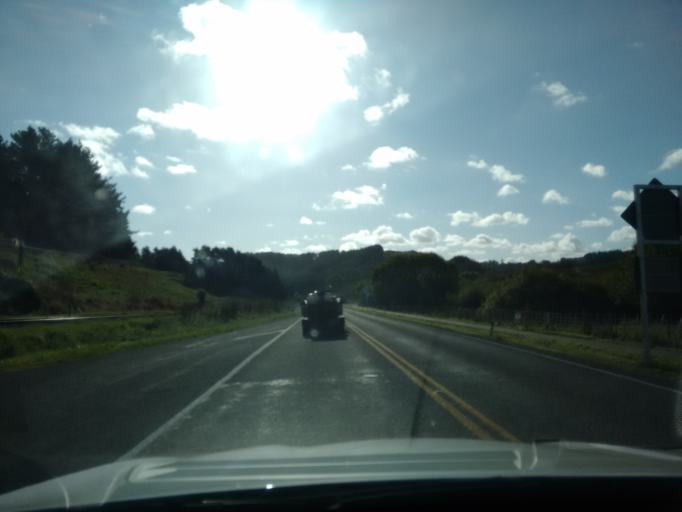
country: NZ
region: Manawatu-Wanganui
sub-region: Wanganui District
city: Wanganui
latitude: -39.8506
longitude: 174.9303
